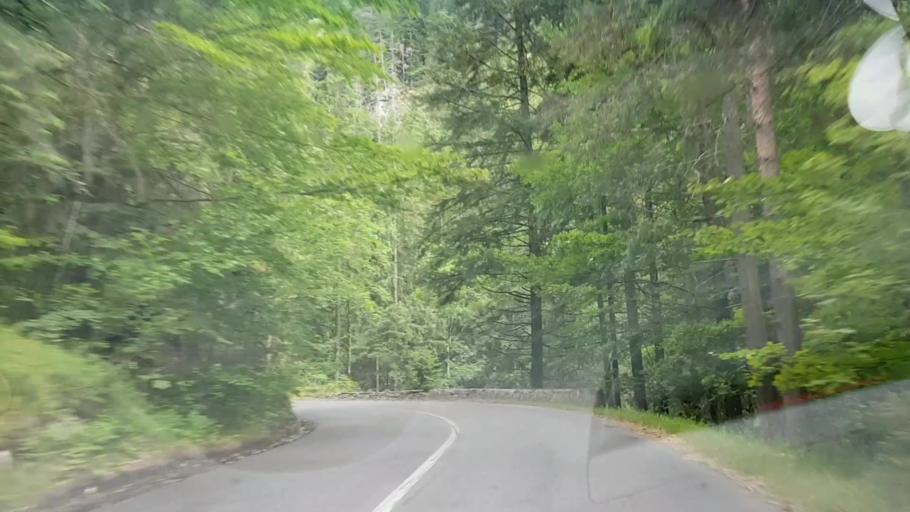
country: RO
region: Neamt
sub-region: Comuna Bicaz Chei
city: Bicaz Chei
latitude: 46.8072
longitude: 25.8119
